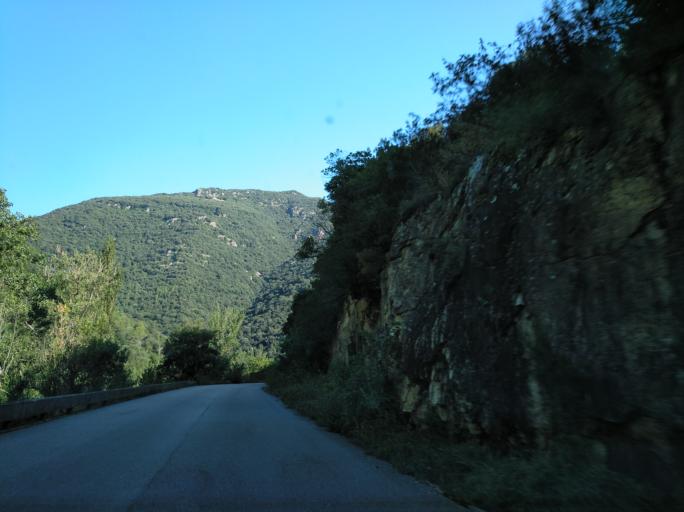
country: ES
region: Catalonia
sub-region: Provincia de Girona
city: Susqueda
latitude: 41.9879
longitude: 2.5706
